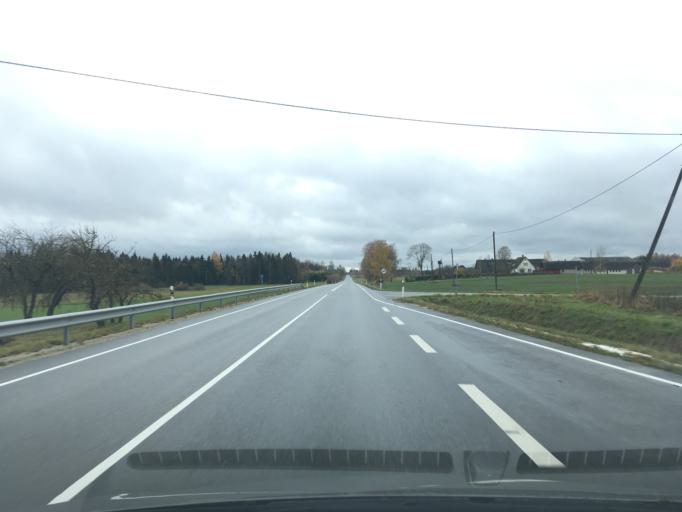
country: EE
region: Jogevamaa
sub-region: Tabivere vald
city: Tabivere
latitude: 58.4567
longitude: 26.5323
